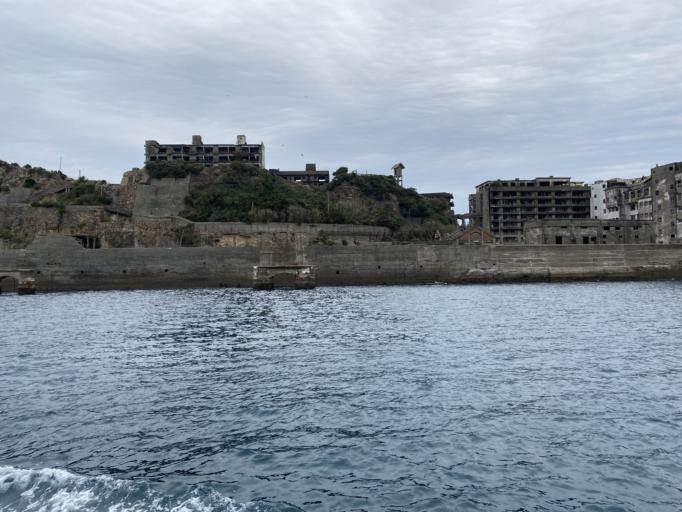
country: JP
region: Nagasaki
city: Nagasaki-shi
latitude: 32.6271
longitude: 129.7402
